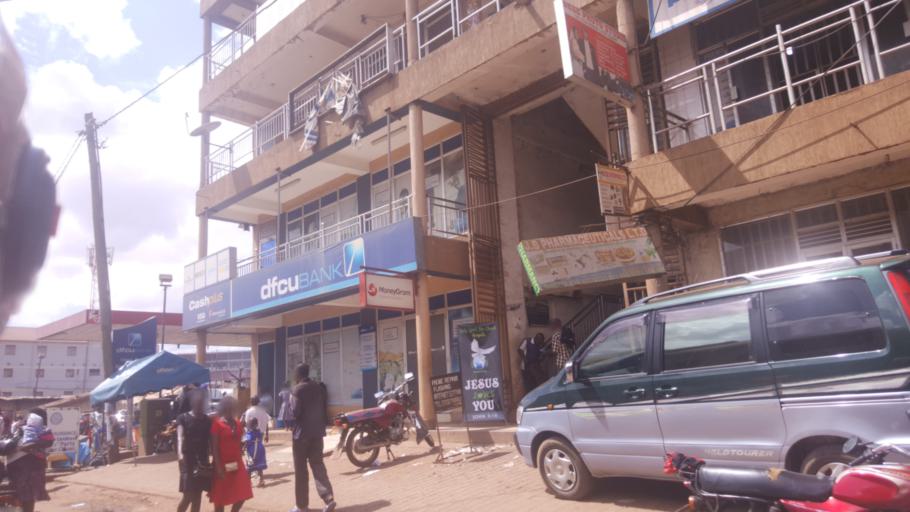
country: UG
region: Central Region
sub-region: Kampala District
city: Kampala
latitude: 0.3098
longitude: 32.5728
